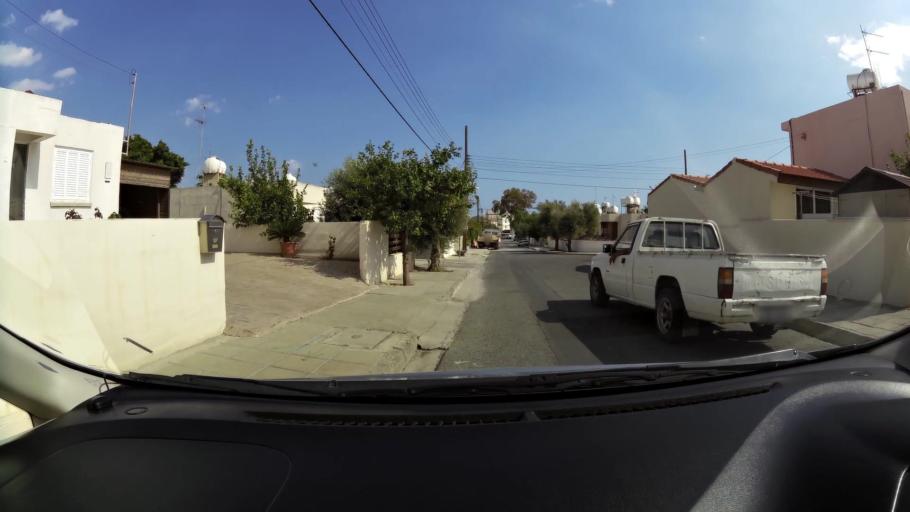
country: CY
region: Larnaka
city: Larnaca
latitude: 34.9078
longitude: 33.5942
